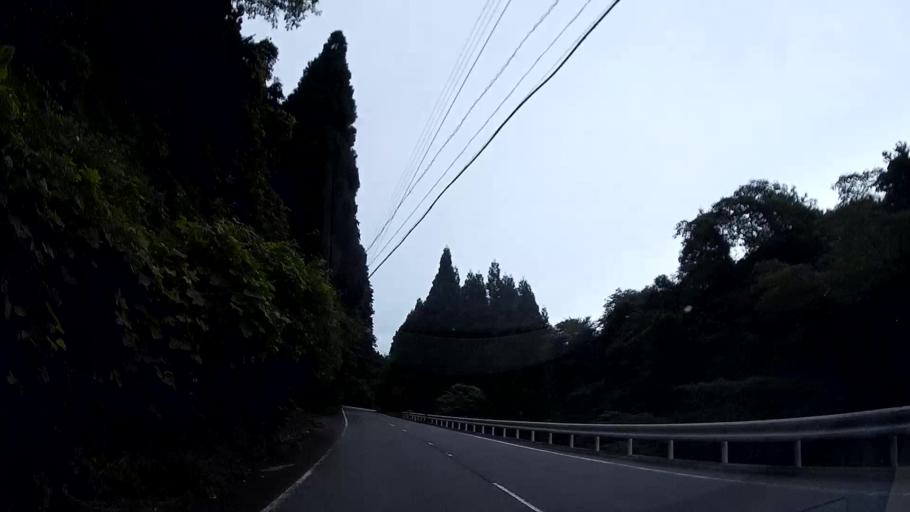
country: JP
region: Kumamoto
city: Kikuchi
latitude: 33.0503
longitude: 130.8968
